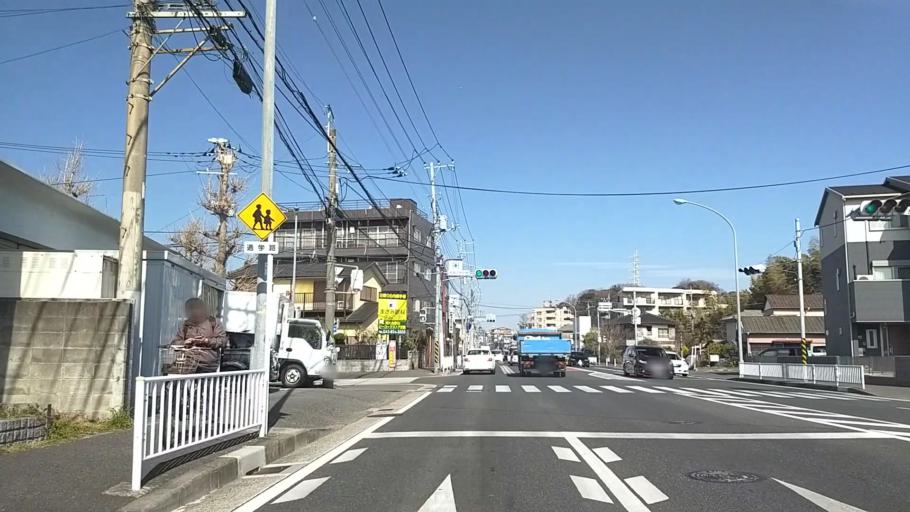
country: JP
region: Kanagawa
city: Yokohama
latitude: 35.3723
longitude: 139.6116
